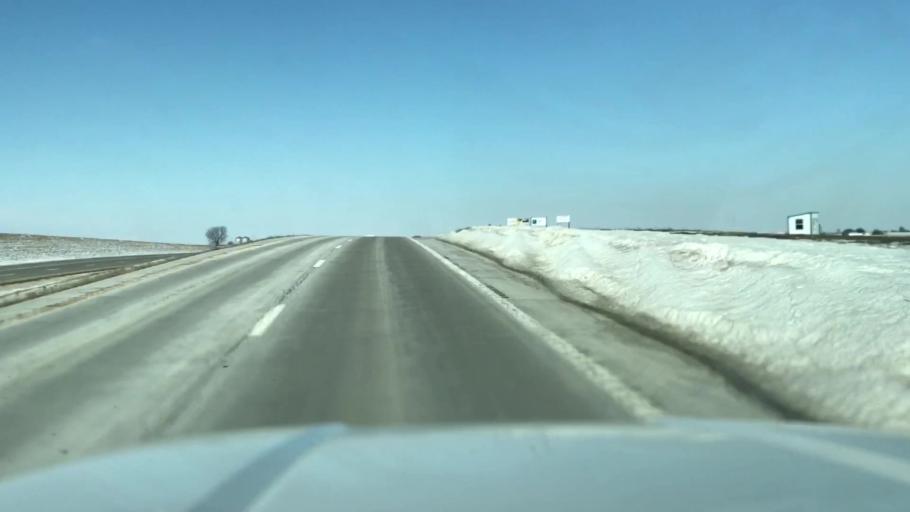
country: US
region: Missouri
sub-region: Andrew County
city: Savannah
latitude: 39.9723
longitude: -94.8733
